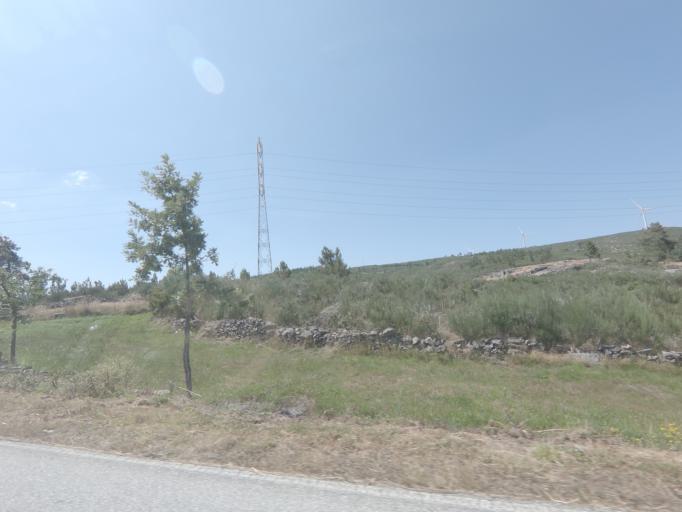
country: PT
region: Viseu
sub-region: Tarouca
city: Tarouca
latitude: 40.9825
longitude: -7.7888
